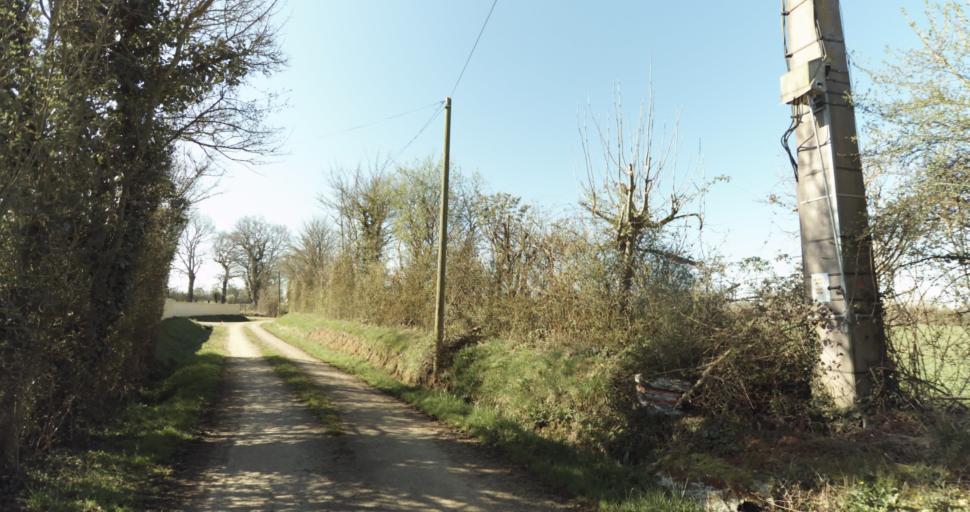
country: FR
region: Lower Normandy
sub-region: Departement du Calvados
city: Saint-Pierre-sur-Dives
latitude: 48.9744
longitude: 0.0023
